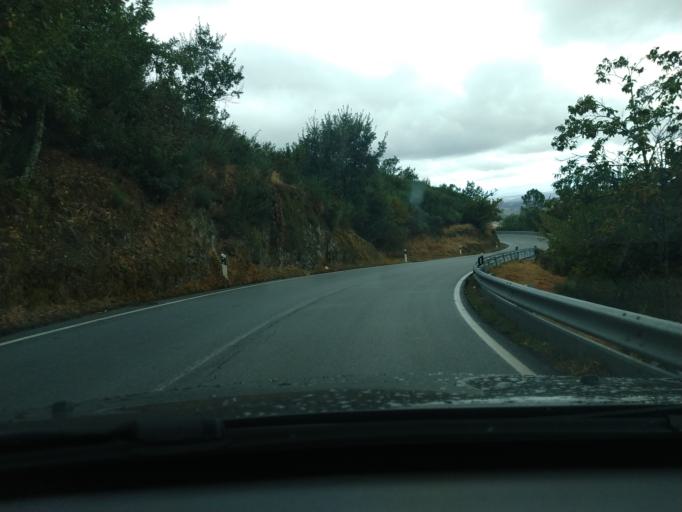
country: PT
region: Guarda
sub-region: Seia
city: Seia
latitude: 40.4135
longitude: -7.6935
